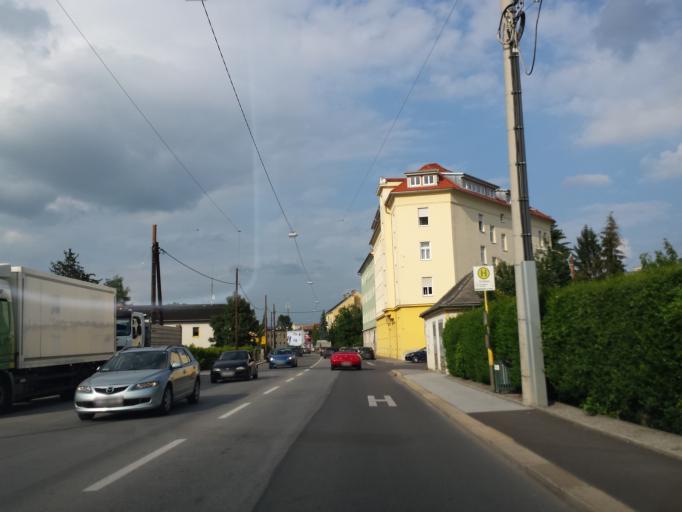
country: AT
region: Styria
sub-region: Graz Stadt
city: Wetzelsdorf
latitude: 47.0612
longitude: 15.3970
